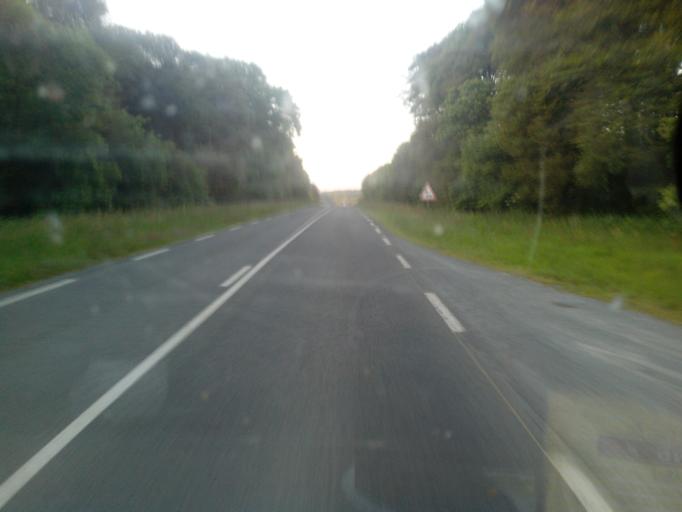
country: FR
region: Brittany
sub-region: Departement d'Ille-et-Vilaine
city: Fougeres
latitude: 48.3790
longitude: -1.1739
